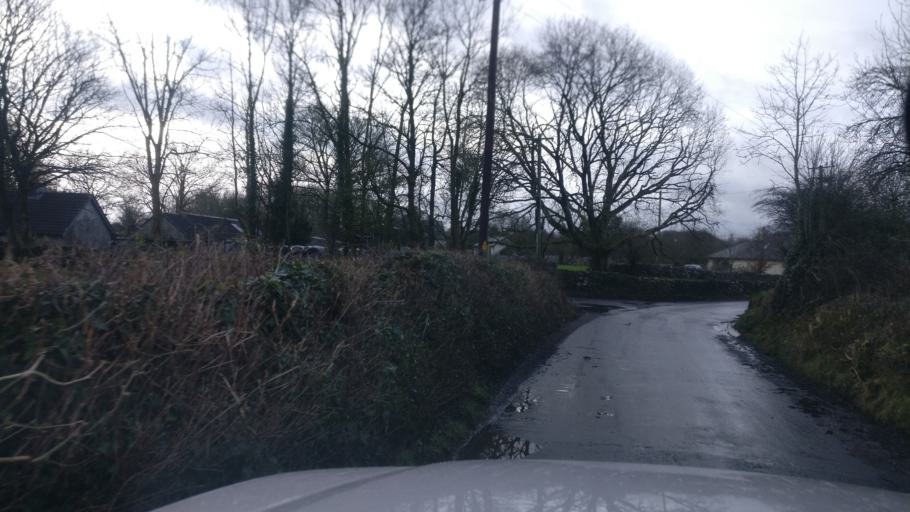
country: IE
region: Connaught
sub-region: County Galway
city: Athenry
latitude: 53.2696
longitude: -8.7730
